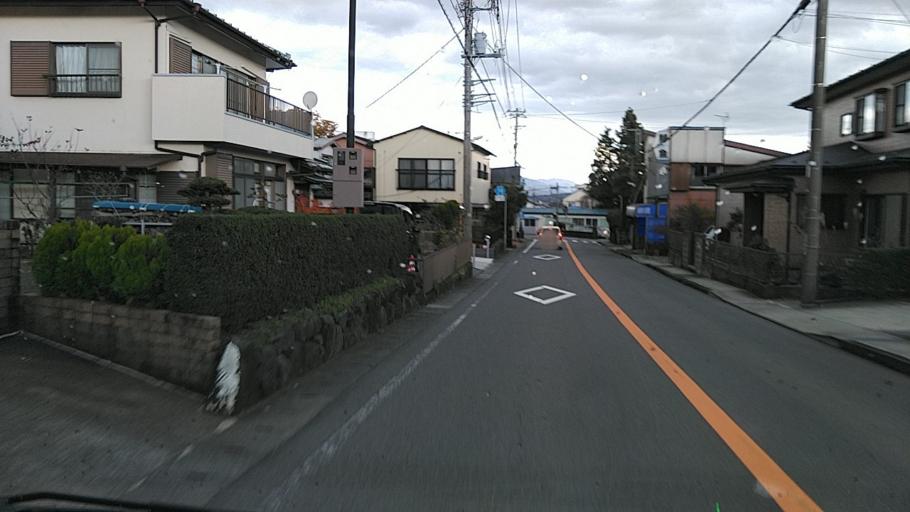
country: JP
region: Shizuoka
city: Gotemba
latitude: 35.3168
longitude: 138.9434
